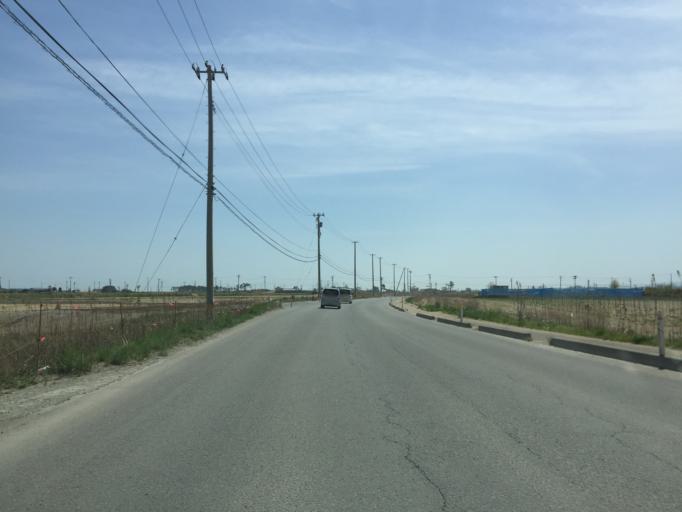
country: JP
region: Miyagi
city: Watari
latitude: 37.9761
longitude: 140.9033
